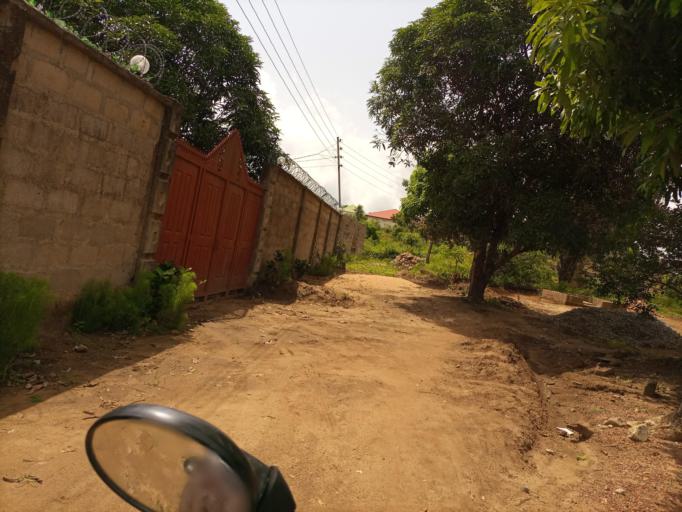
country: SL
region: Southern Province
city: Bo
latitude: 7.9733
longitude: -11.7666
